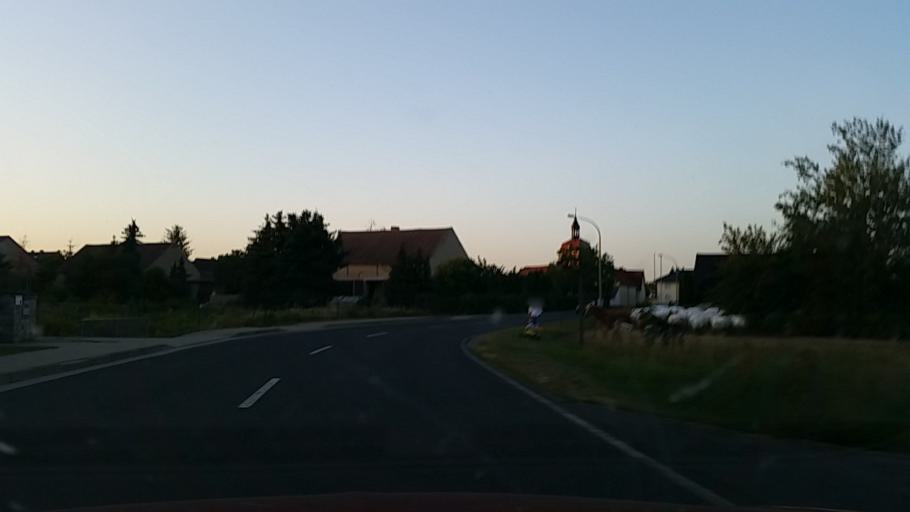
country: DE
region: Saxony-Anhalt
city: Prettin
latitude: 51.7190
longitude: 12.9357
